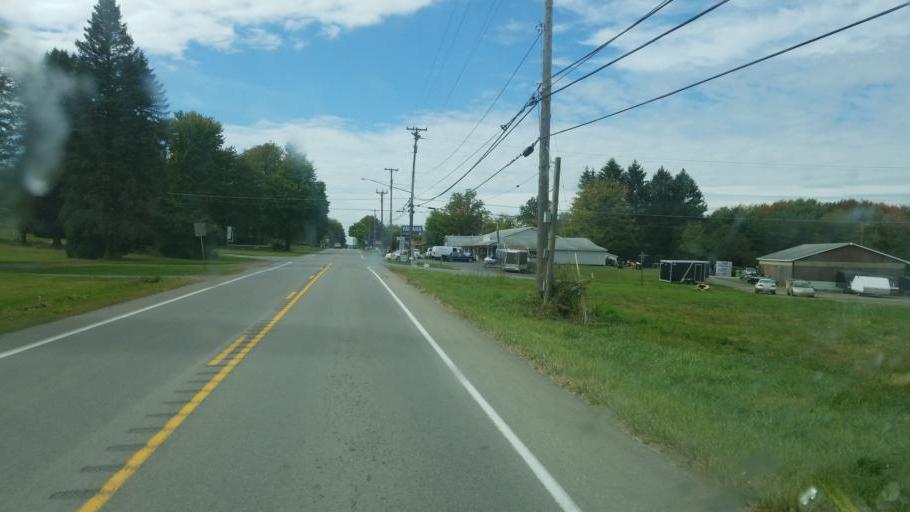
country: US
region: Pennsylvania
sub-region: Mercer County
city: Greenville
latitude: 41.4173
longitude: -80.3374
